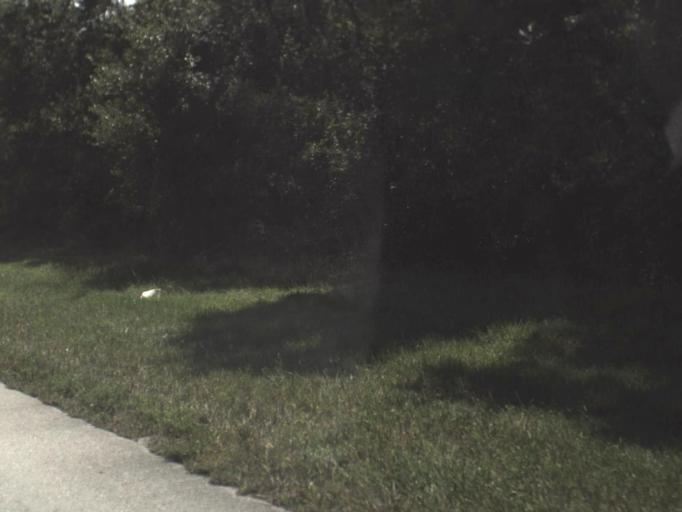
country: US
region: Florida
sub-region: DeSoto County
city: Arcadia
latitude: 27.2299
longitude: -81.8948
